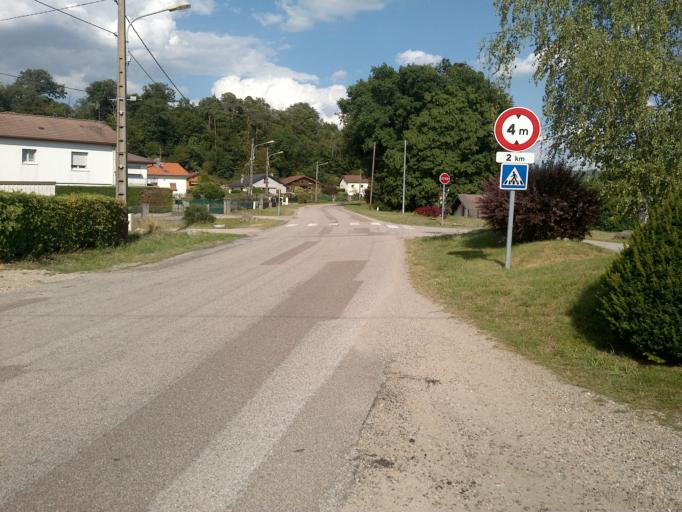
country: FR
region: Lorraine
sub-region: Departement des Vosges
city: Archettes
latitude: 48.1223
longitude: 6.5403
